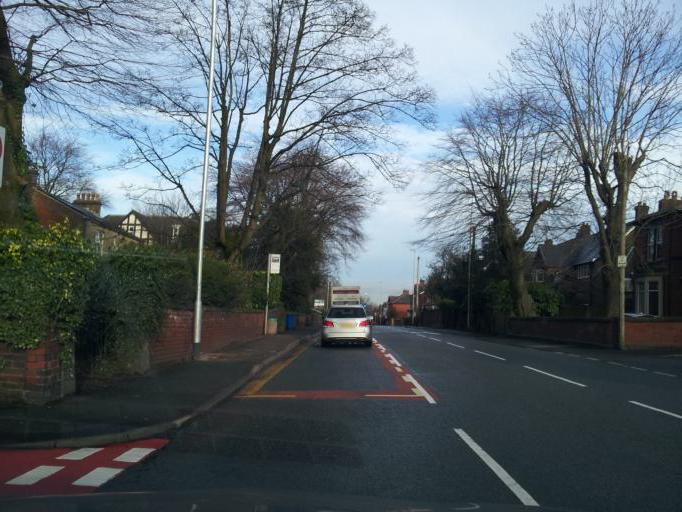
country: GB
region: England
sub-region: Manchester
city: Heywood
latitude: 53.5806
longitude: -2.2137
